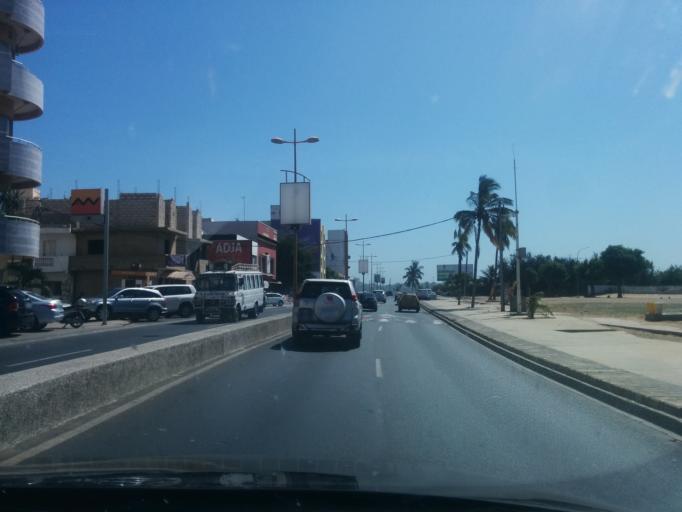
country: SN
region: Dakar
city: Dakar
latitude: 14.6761
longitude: -17.4540
